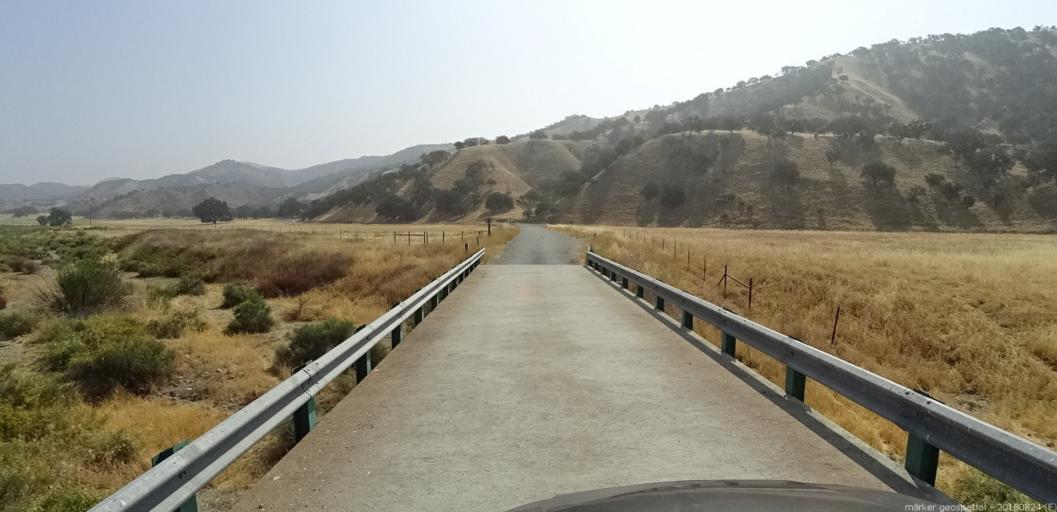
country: US
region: California
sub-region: San Luis Obispo County
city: San Miguel
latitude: 35.9073
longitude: -120.6936
